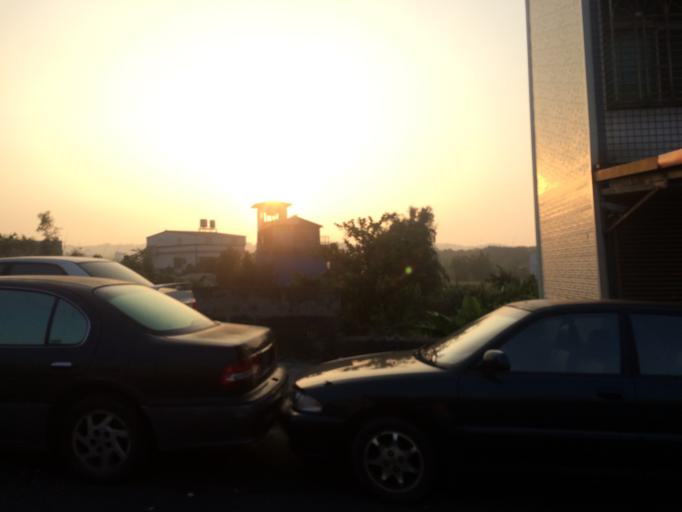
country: TW
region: Taiwan
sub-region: Hsinchu
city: Hsinchu
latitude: 24.7347
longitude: 120.9128
